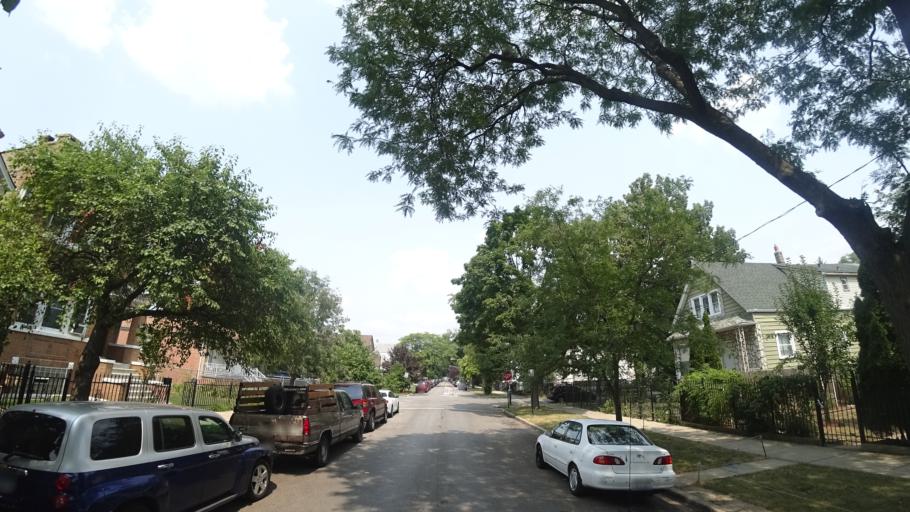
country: US
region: Illinois
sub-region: Cook County
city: Cicero
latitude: 41.8381
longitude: -87.7329
